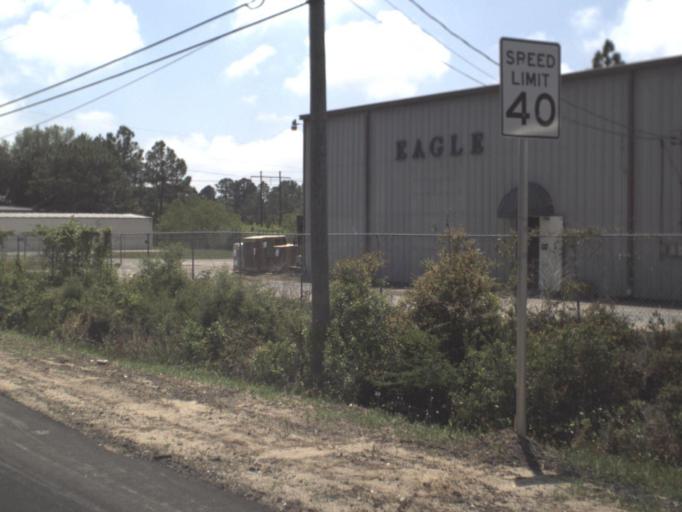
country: US
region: Florida
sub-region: Escambia County
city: Myrtle Grove
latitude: 30.3935
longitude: -87.3130
